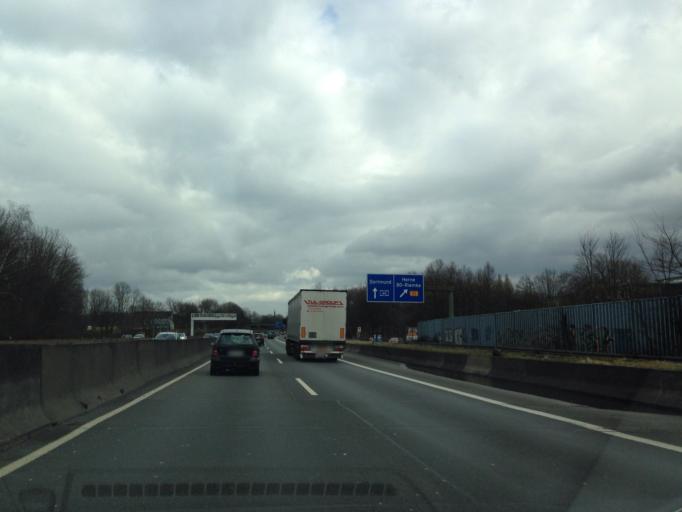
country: DE
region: North Rhine-Westphalia
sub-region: Regierungsbezirk Arnsberg
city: Bochum
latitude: 51.4980
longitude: 7.2120
